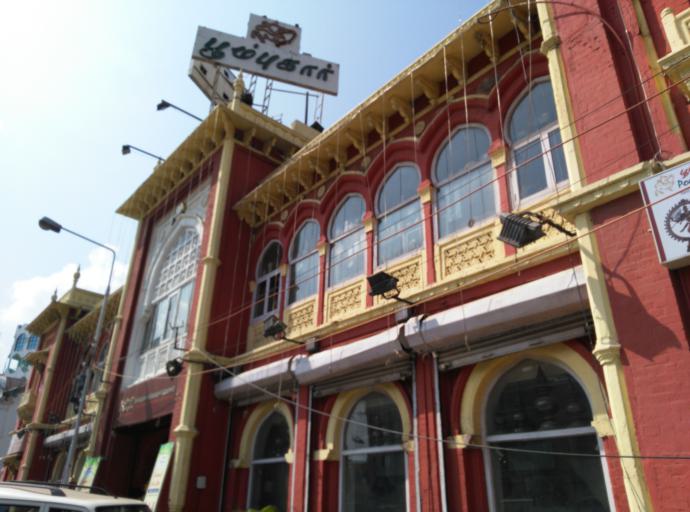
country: IN
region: Tamil Nadu
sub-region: Chennai
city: Chennai
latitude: 13.0655
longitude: 80.2671
